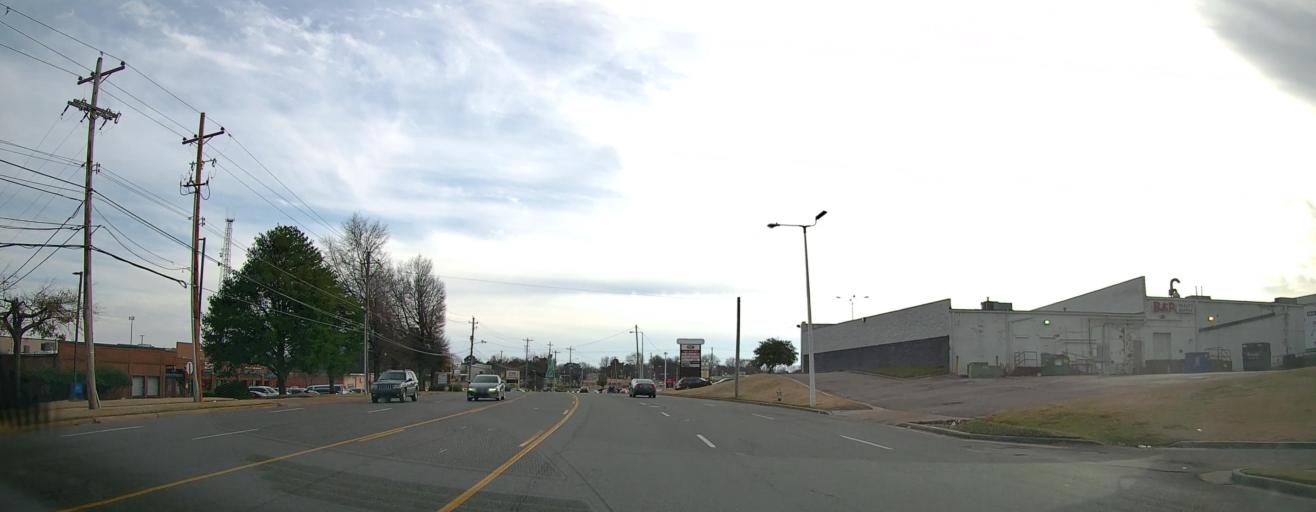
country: US
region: Tennessee
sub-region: Shelby County
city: Germantown
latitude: 35.0523
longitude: -89.8440
